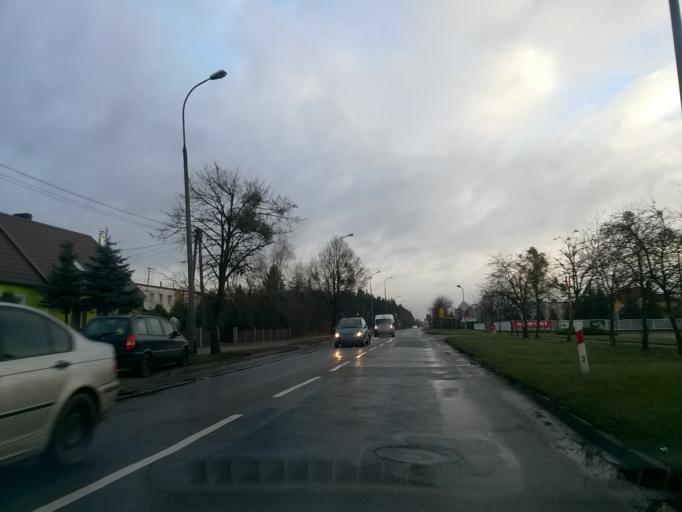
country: PL
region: Greater Poland Voivodeship
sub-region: Powiat wagrowiecki
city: Wagrowiec
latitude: 52.8157
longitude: 17.2179
